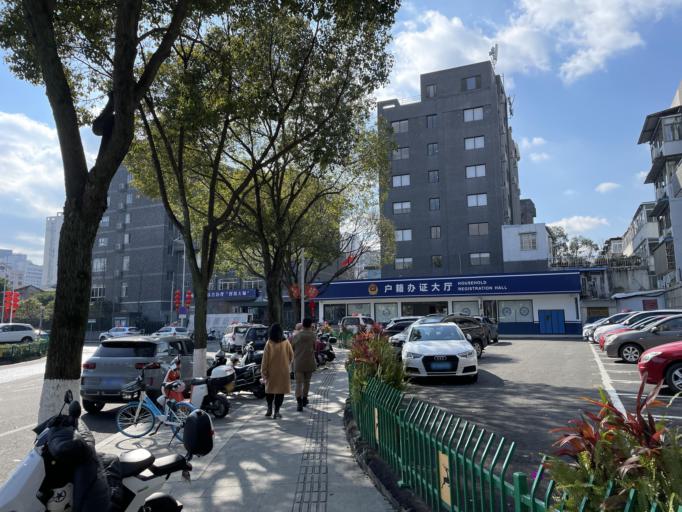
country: CN
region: Zhejiang Sheng
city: Wuma
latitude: 28.0202
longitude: 120.6527
